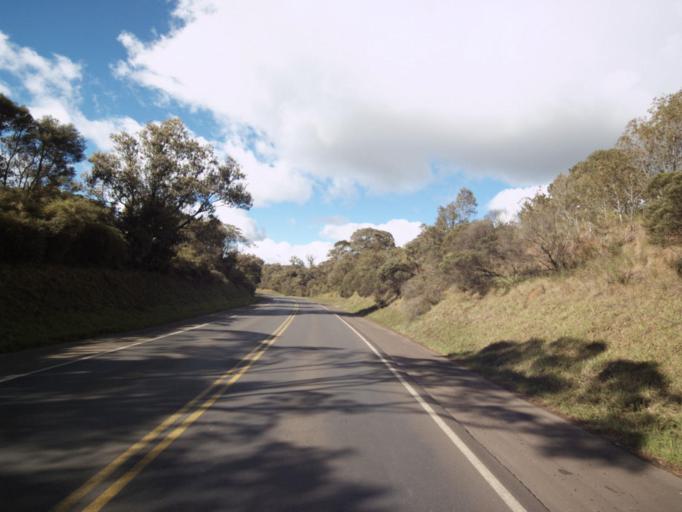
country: BR
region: Santa Catarina
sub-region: Joacaba
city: Joacaba
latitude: -26.9762
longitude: -51.7727
